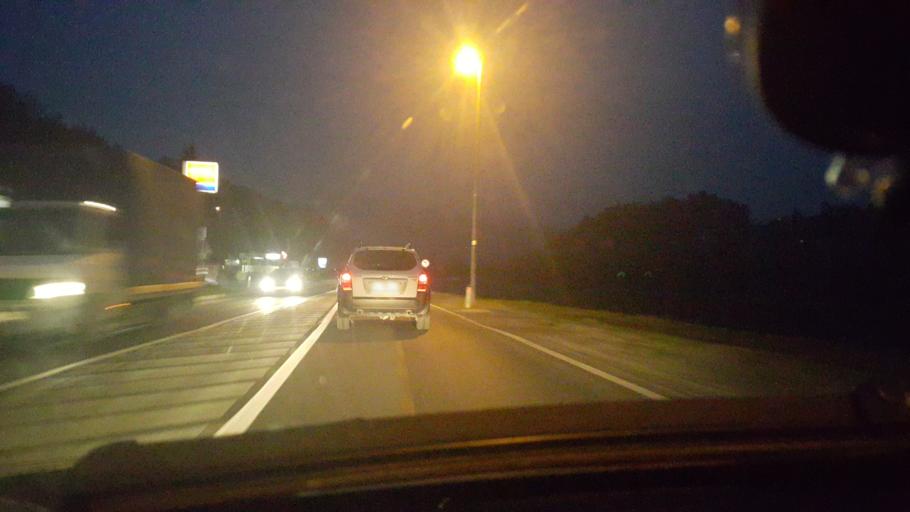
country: SI
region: Muta
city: Muta
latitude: 46.6041
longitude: 15.1642
